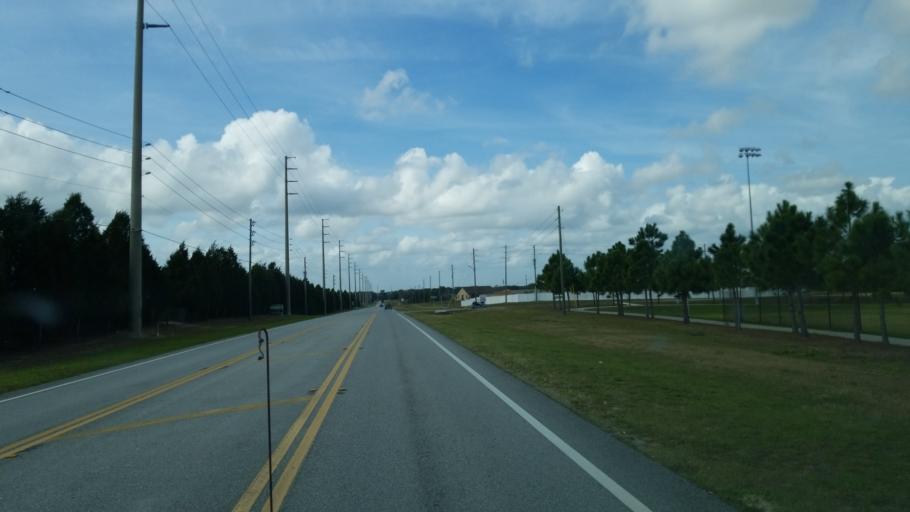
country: US
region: Florida
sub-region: Polk County
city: Dundee
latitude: 28.0269
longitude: -81.5029
